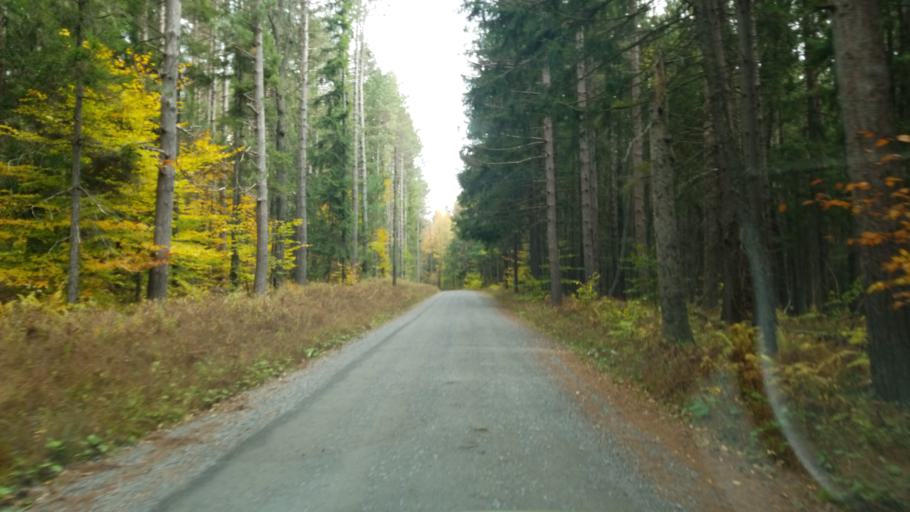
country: US
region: Pennsylvania
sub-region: Clearfield County
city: Clearfield
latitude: 41.2020
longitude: -78.4275
